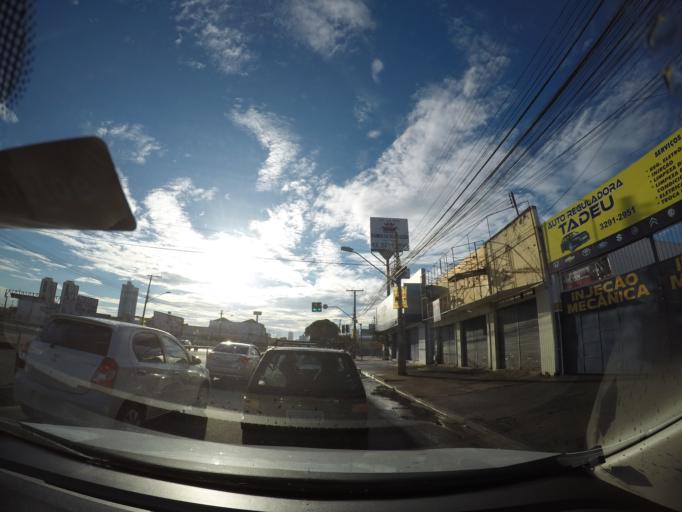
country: BR
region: Goias
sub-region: Goiania
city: Goiania
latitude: -16.6744
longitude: -49.2829
